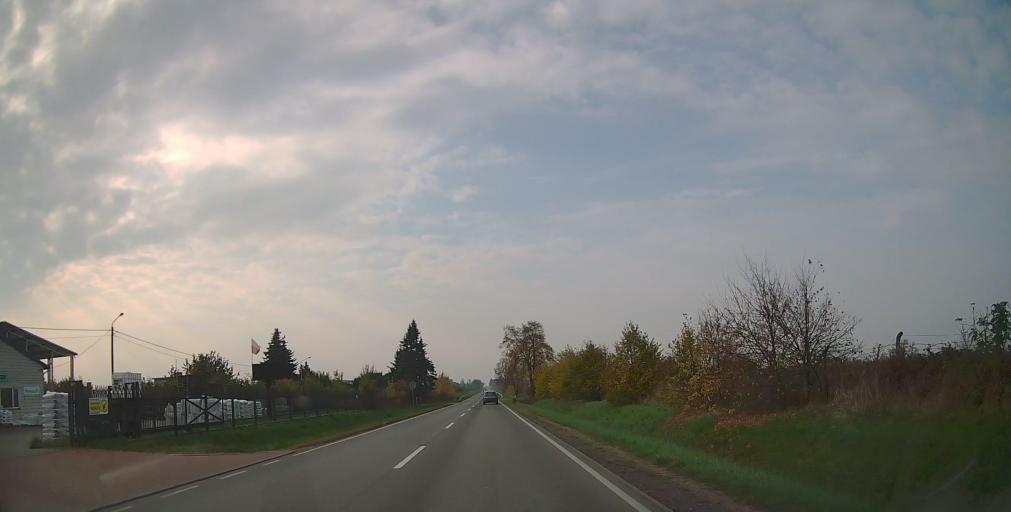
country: PL
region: Masovian Voivodeship
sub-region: Powiat grojecki
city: Belsk Duzy
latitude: 51.7850
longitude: 20.7778
